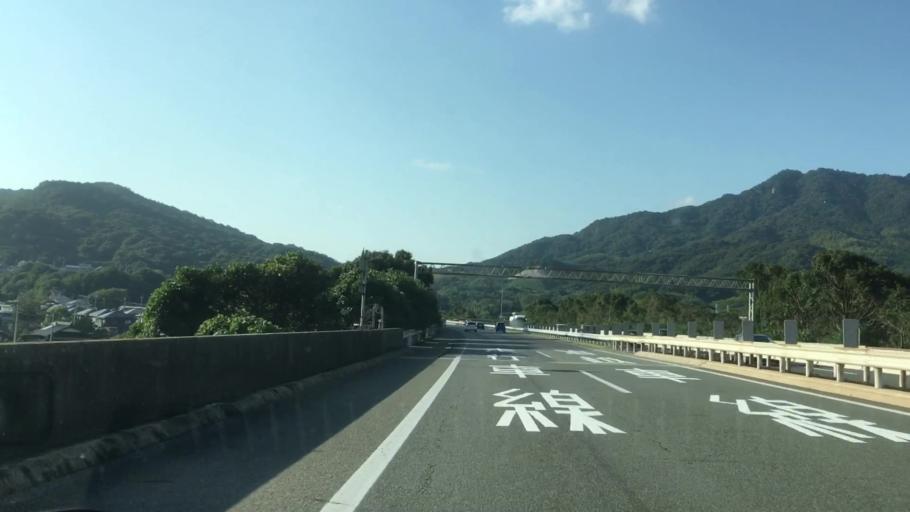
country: JP
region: Yamaguchi
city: Hofu
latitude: 34.0662
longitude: 131.6039
